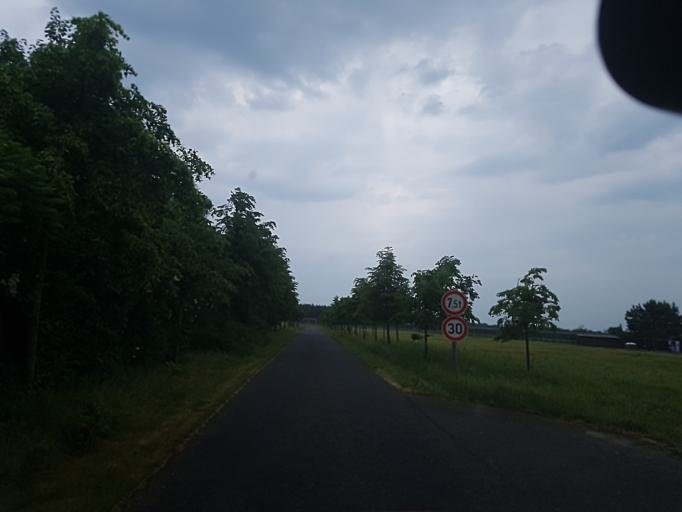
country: DE
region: Saxony-Anhalt
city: Elster
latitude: 51.8195
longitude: 12.8617
